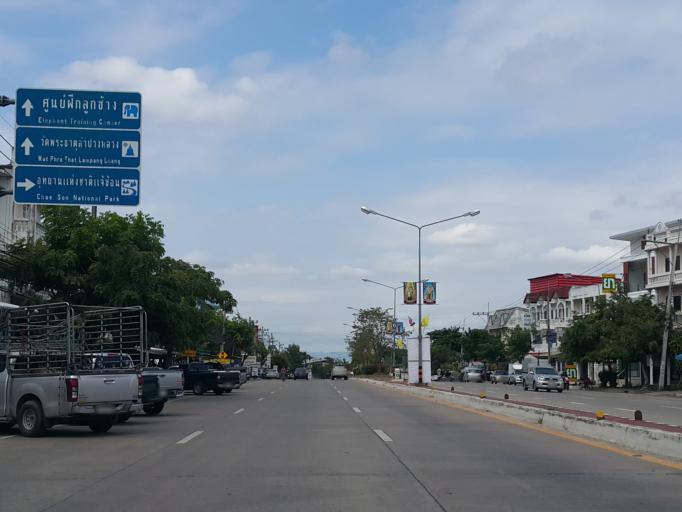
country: TH
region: Lampang
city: Lampang
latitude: 18.3089
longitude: 99.4665
